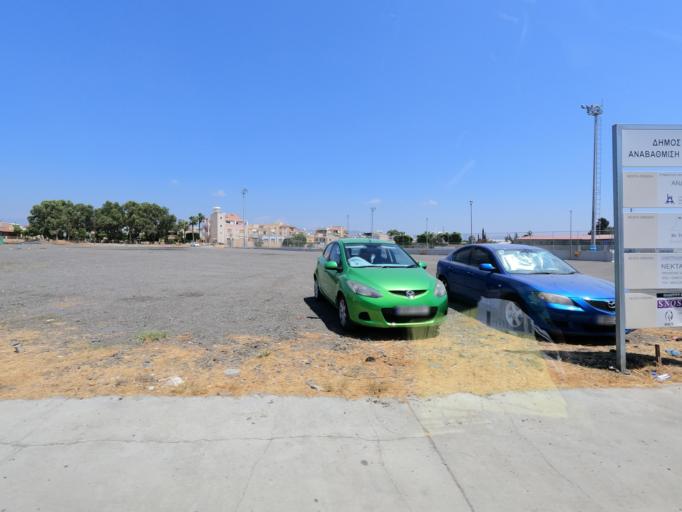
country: CY
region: Limassol
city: Limassol
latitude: 34.6763
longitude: 33.0161
